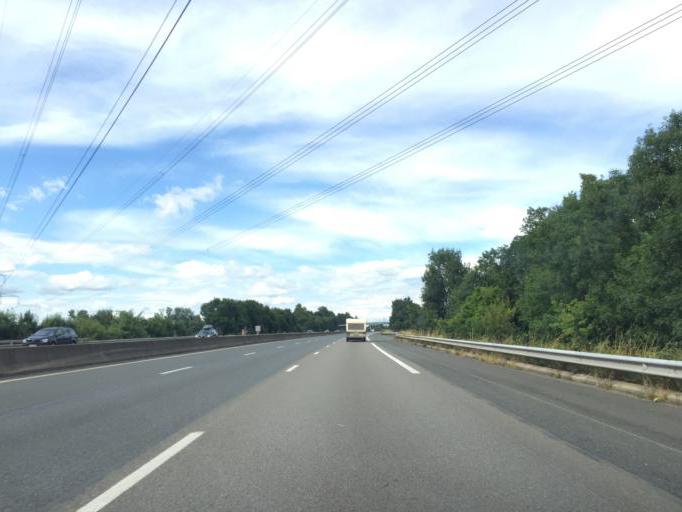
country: FR
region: Bourgogne
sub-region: Departement de Saone-et-Loire
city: Romaneche-Thorins
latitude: 46.1804
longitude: 4.7706
